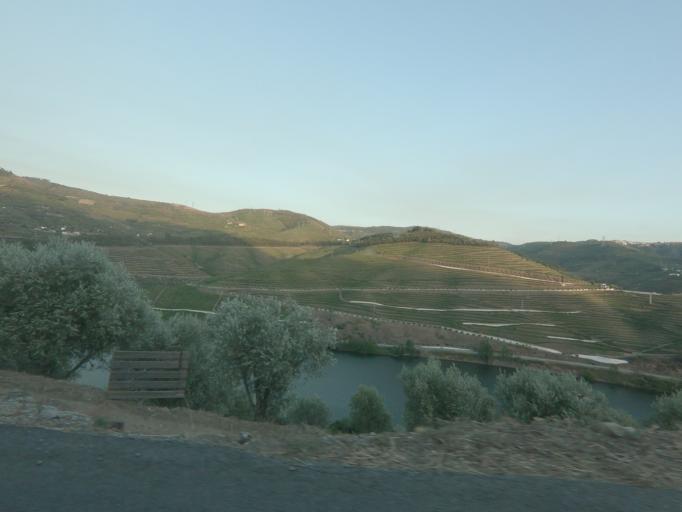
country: PT
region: Viseu
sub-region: Armamar
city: Armamar
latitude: 41.1458
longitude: -7.6945
